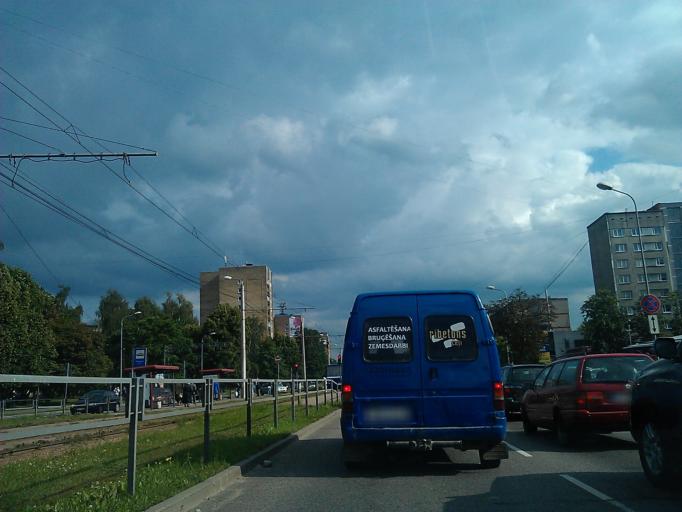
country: LV
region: Kekava
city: Balozi
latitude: 56.9186
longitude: 24.1730
